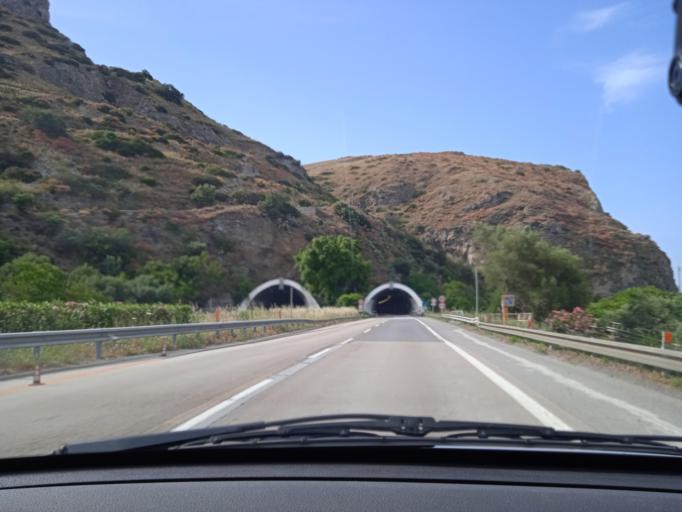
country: IT
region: Sicily
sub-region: Messina
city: Oliveri
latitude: 38.1319
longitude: 15.0524
